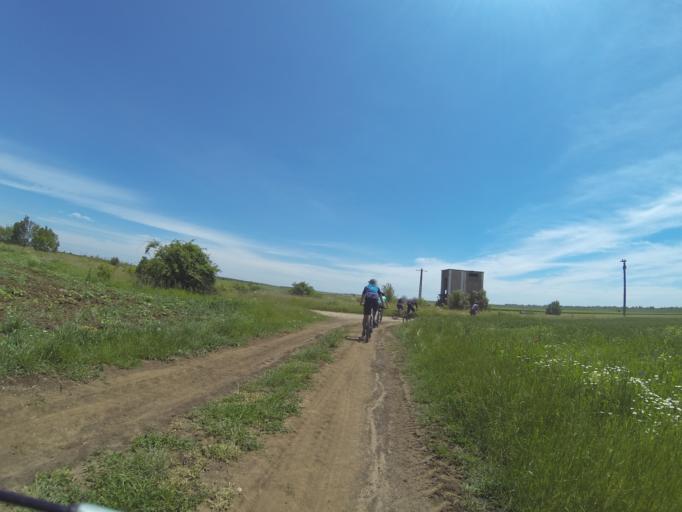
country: RO
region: Dolj
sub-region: Comuna Leu
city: Zanoaga
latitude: 44.1750
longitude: 24.0921
